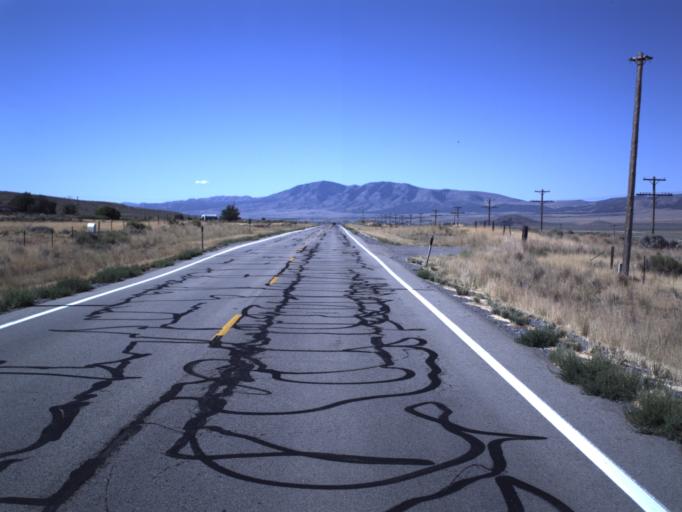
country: US
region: Utah
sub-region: Tooele County
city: Tooele
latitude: 40.4429
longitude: -112.3678
